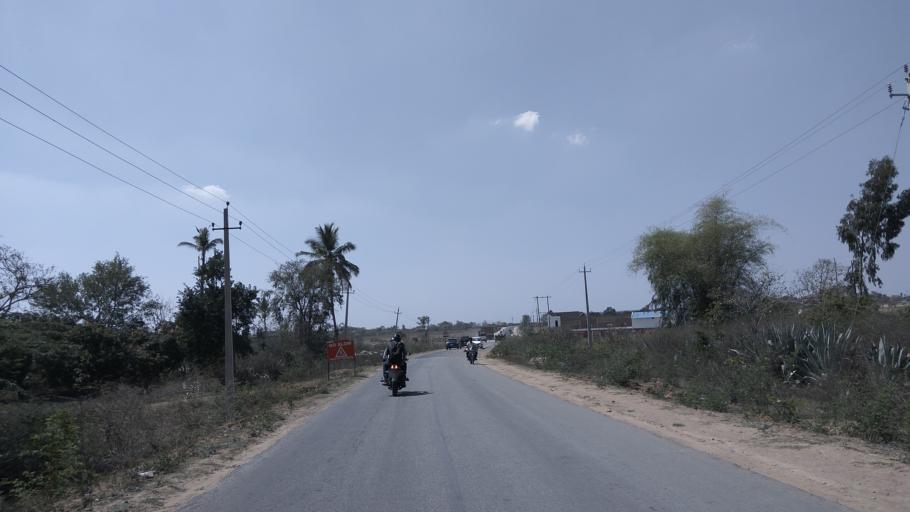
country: IN
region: Karnataka
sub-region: Kolar
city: Mulbagal
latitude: 13.1684
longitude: 78.3622
